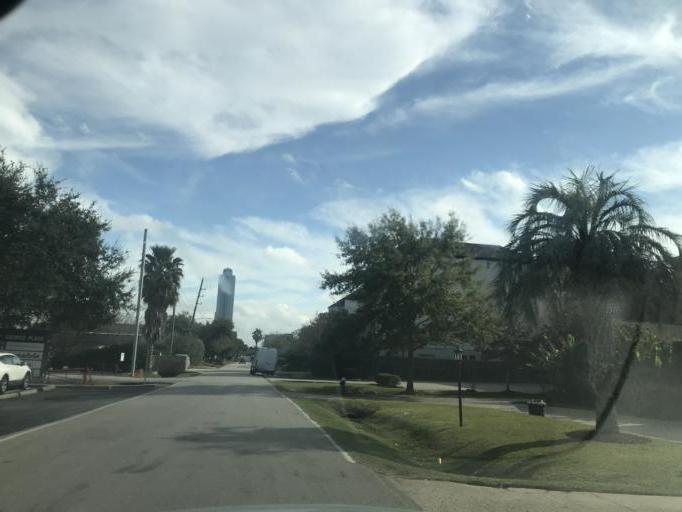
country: US
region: Texas
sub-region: Harris County
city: Bellaire
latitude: 29.7365
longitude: -95.4797
